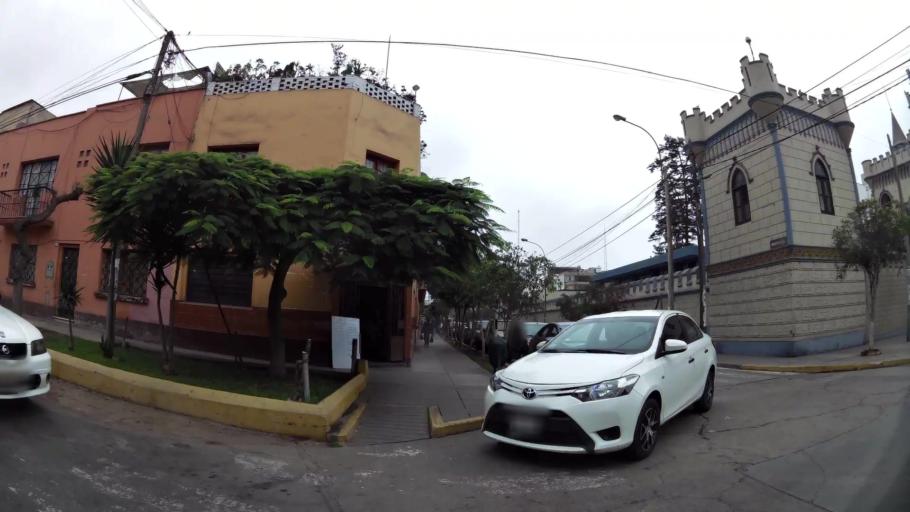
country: PE
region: Lima
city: Lima
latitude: -12.0782
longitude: -77.0327
